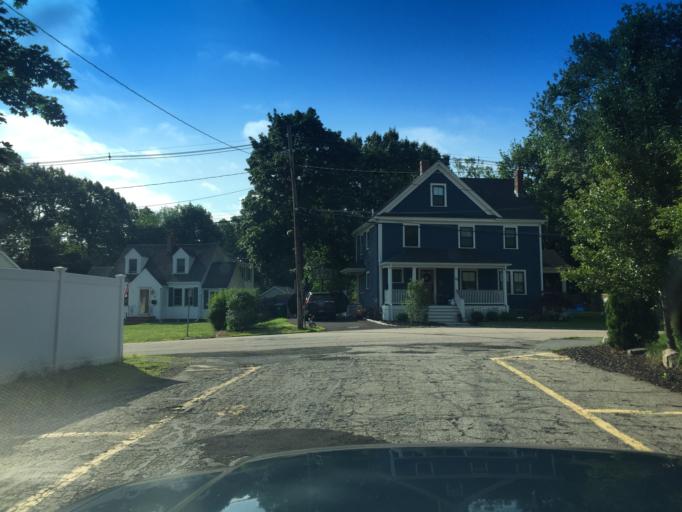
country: US
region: Massachusetts
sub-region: Norfolk County
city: Dedham
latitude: 42.2208
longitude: -71.1838
